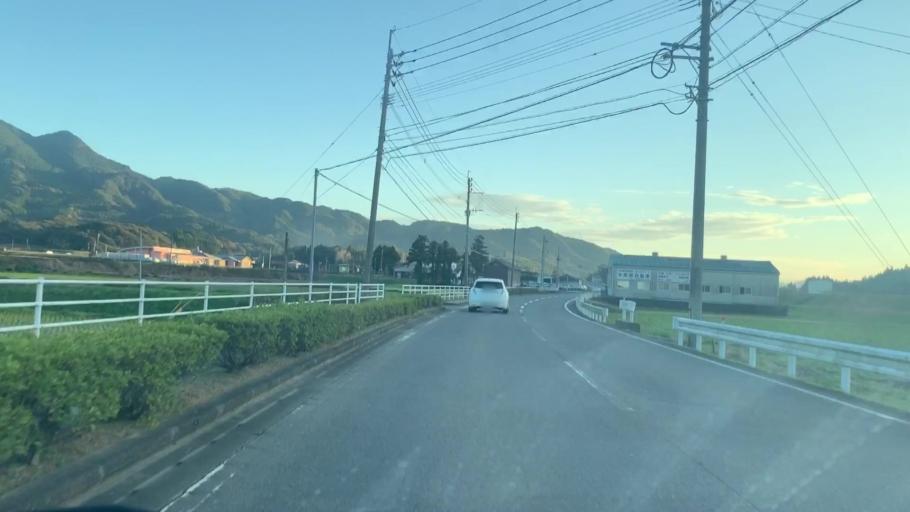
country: JP
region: Saga Prefecture
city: Imaricho-ko
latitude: 33.2979
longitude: 129.9702
